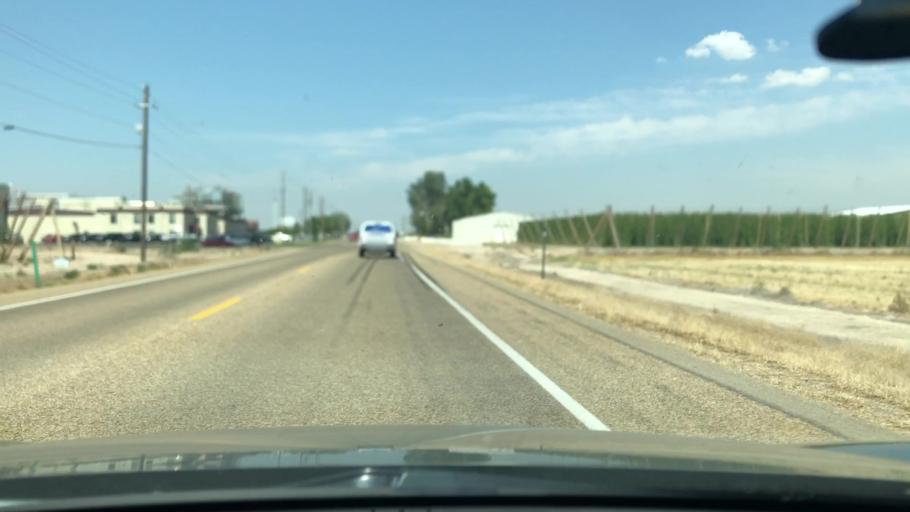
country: US
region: Idaho
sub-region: Canyon County
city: Wilder
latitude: 43.6934
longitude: -116.9120
